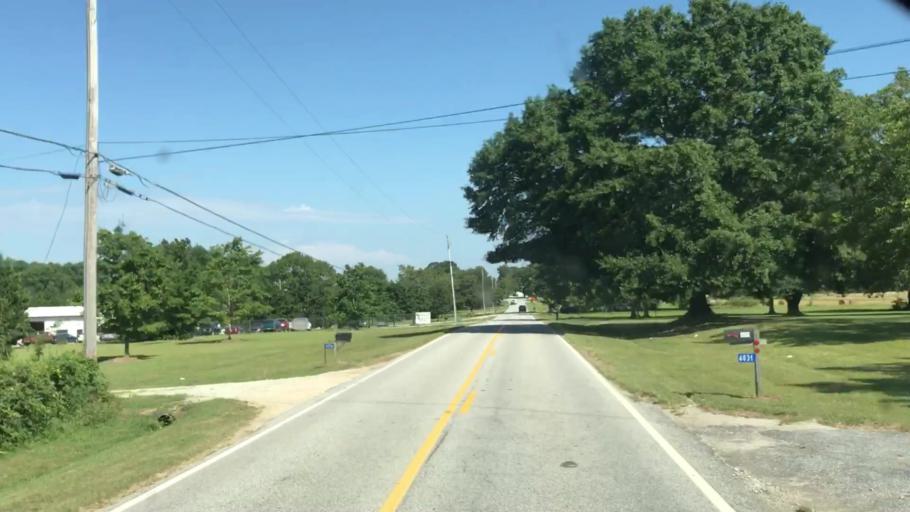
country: US
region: Georgia
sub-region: Walton County
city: Loganville
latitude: 33.8473
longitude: -83.8584
